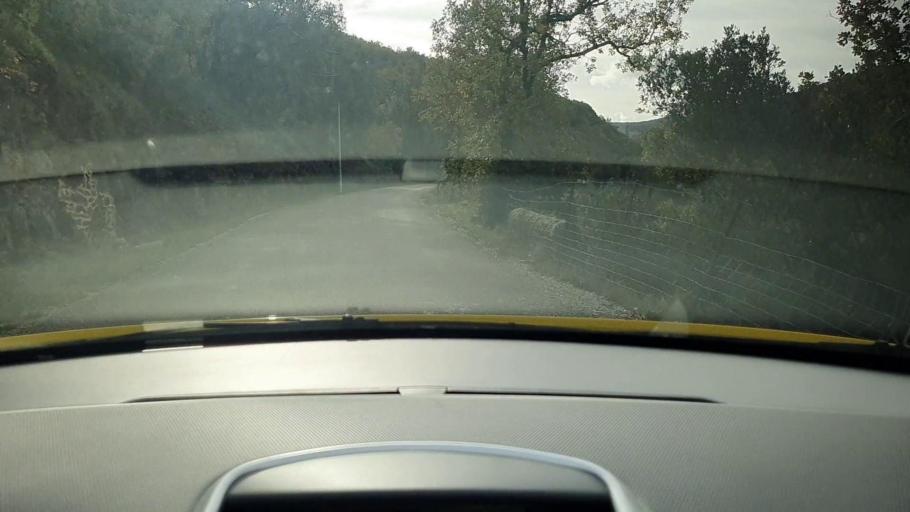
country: FR
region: Languedoc-Roussillon
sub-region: Departement du Gard
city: Saint-Jean-du-Gard
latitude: 44.0608
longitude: 3.9238
